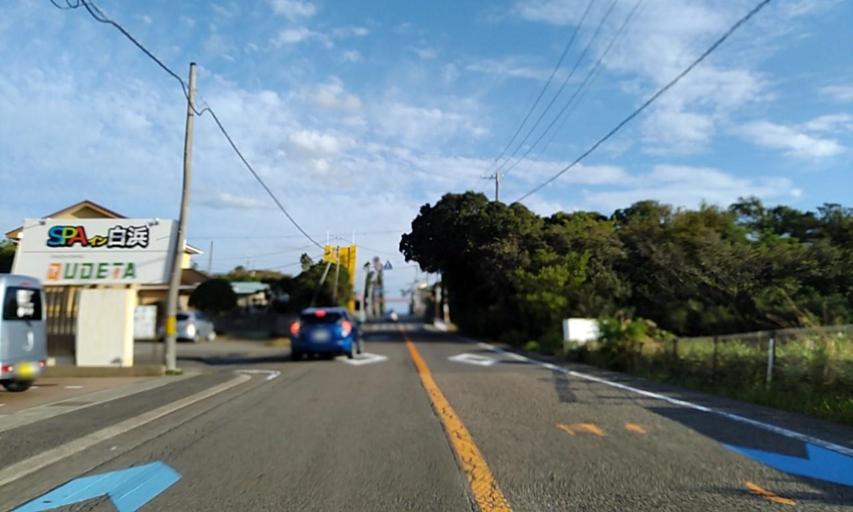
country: JP
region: Wakayama
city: Tanabe
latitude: 33.6672
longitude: 135.3357
